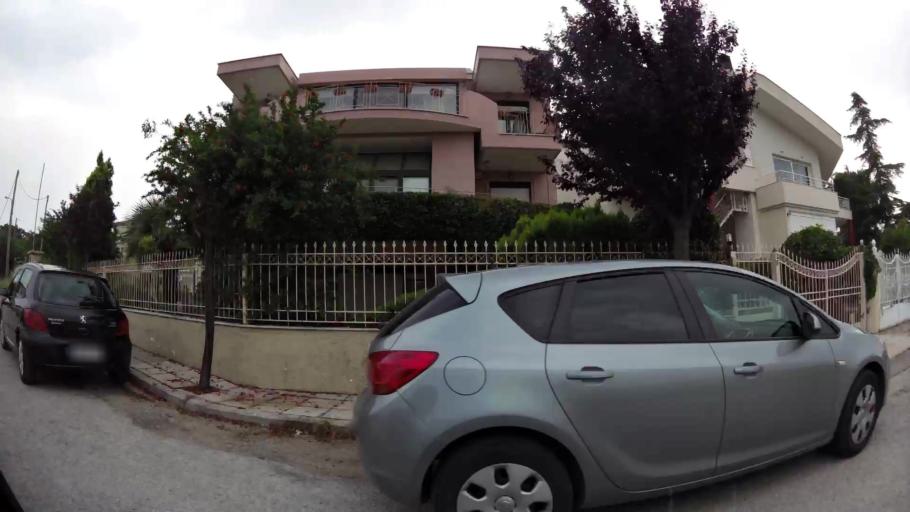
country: GR
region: Central Macedonia
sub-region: Nomos Thessalonikis
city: Oraiokastro
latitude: 40.7135
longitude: 22.9320
